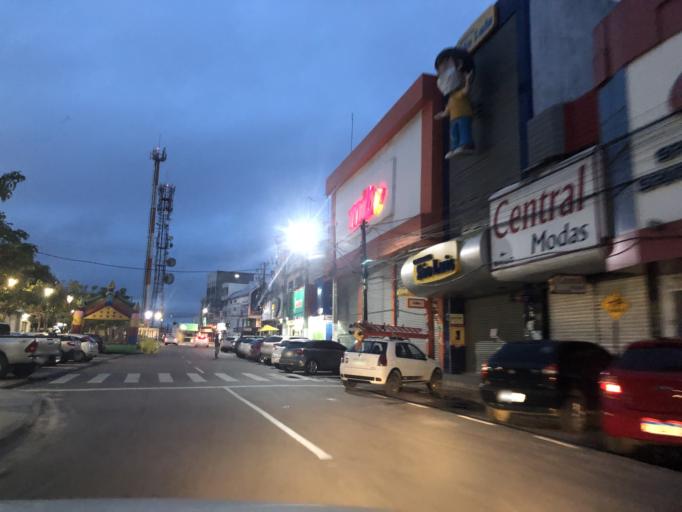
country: BR
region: Bahia
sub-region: Santo Antonio De Jesus
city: Santo Antonio de Jesus
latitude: -12.9683
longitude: -39.2626
